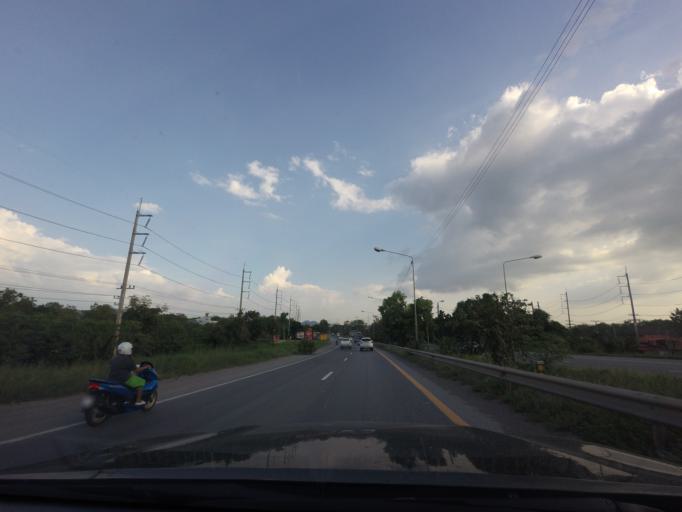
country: TH
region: Sara Buri
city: Saraburi
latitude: 14.5235
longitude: 100.8887
